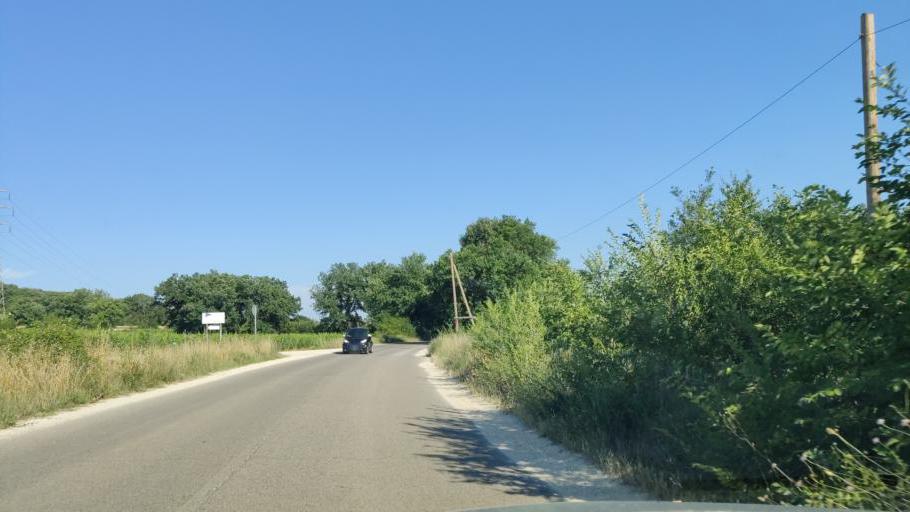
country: IT
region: Latium
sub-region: Provincia di Viterbo
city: Orte
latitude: 42.4731
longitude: 12.3678
